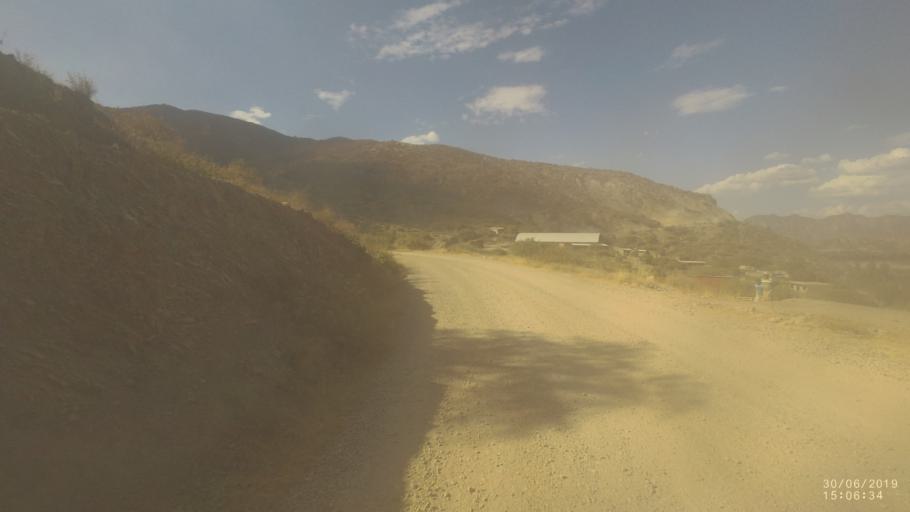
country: BO
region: Cochabamba
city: Irpa Irpa
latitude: -17.7317
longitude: -66.3104
